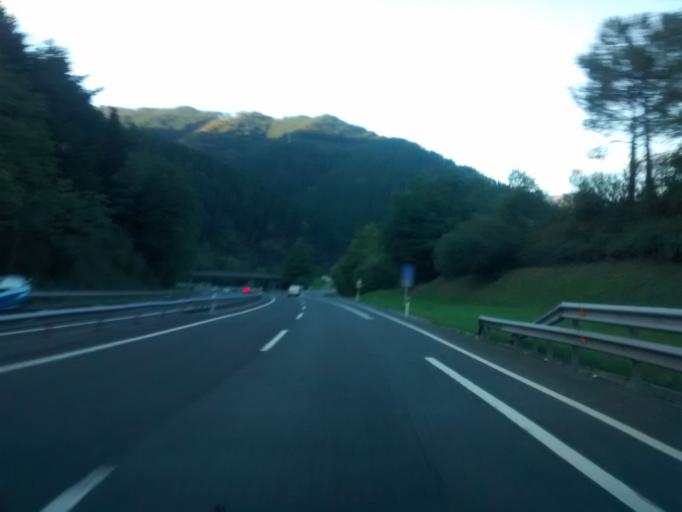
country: ES
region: Basque Country
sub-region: Provincia de Guipuzcoa
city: Elgoibar
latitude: 43.2293
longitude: -2.4030
